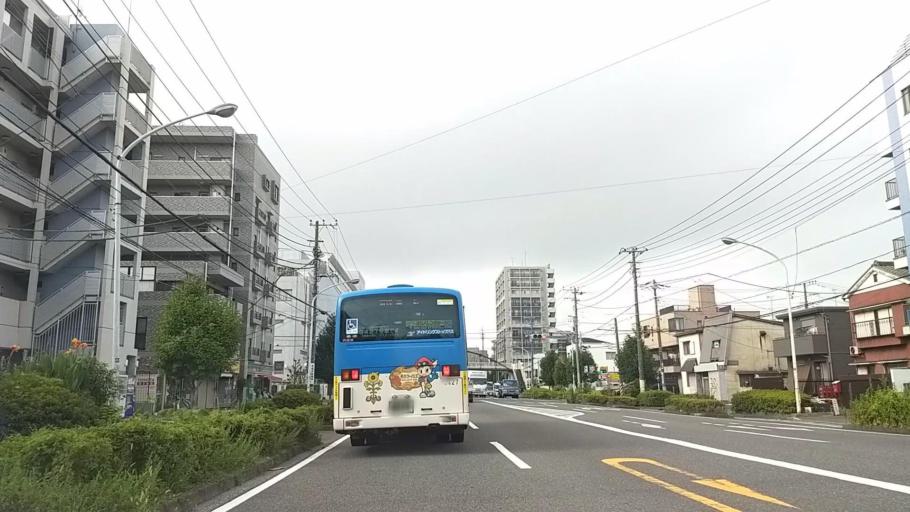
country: JP
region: Kanagawa
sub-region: Kawasaki-shi
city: Kawasaki
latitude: 35.5288
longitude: 139.7140
